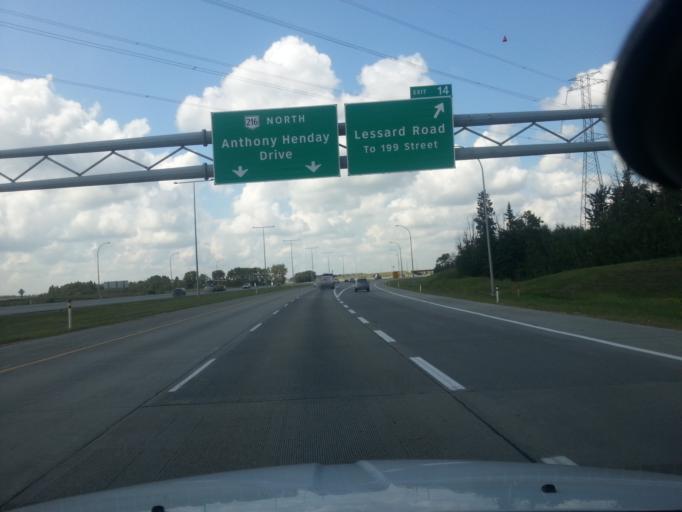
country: CA
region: Alberta
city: Devon
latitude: 53.4730
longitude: -113.6511
